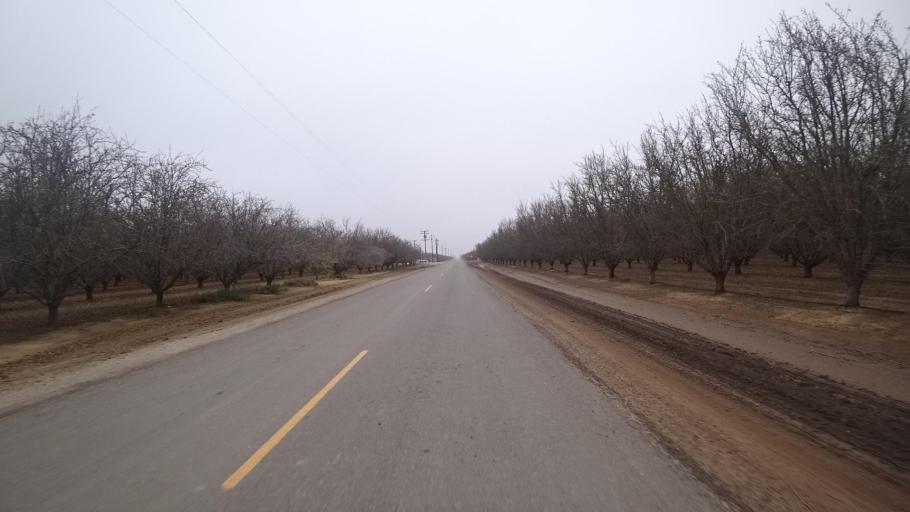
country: US
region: California
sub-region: Kern County
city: Wasco
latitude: 35.5851
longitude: -119.5093
